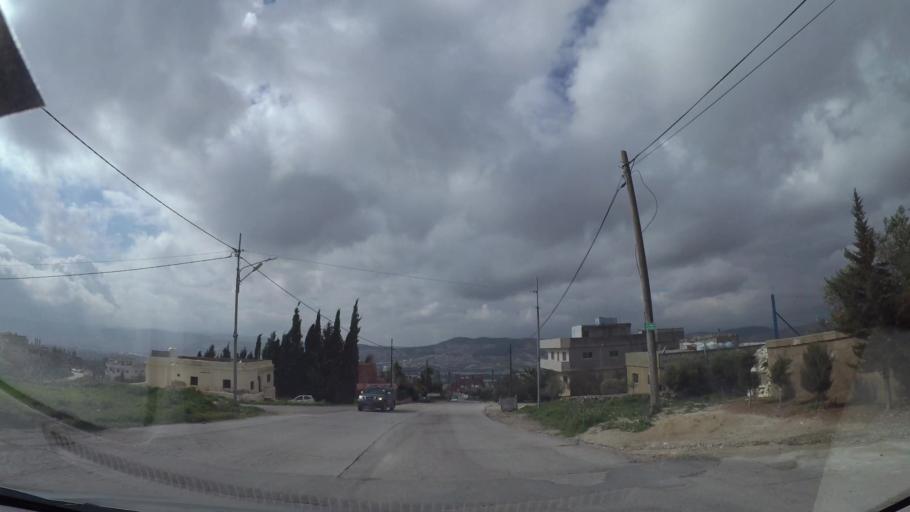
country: JO
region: Amman
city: Al Jubayhah
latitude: 32.0745
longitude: 35.8685
